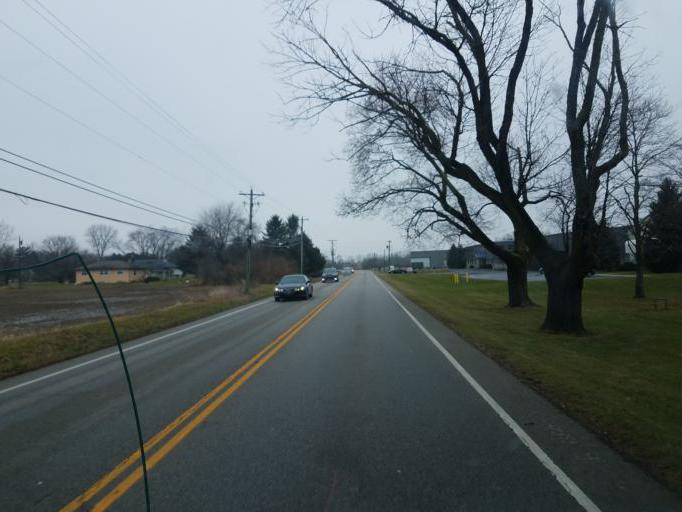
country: US
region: Ohio
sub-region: Union County
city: New California
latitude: 40.1261
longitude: -83.1966
